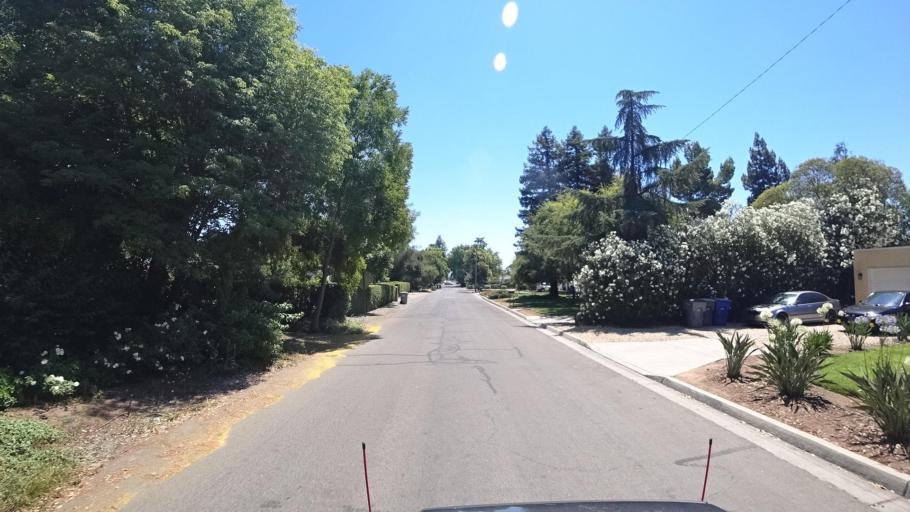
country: US
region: California
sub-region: Fresno County
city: Fresno
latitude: 36.7904
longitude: -119.8018
